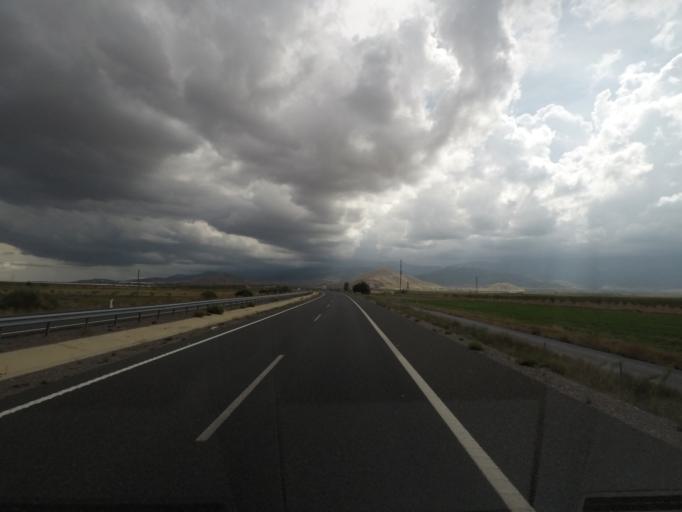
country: ES
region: Andalusia
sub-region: Provincia de Granada
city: Aldeire
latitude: 37.2149
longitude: -3.0721
